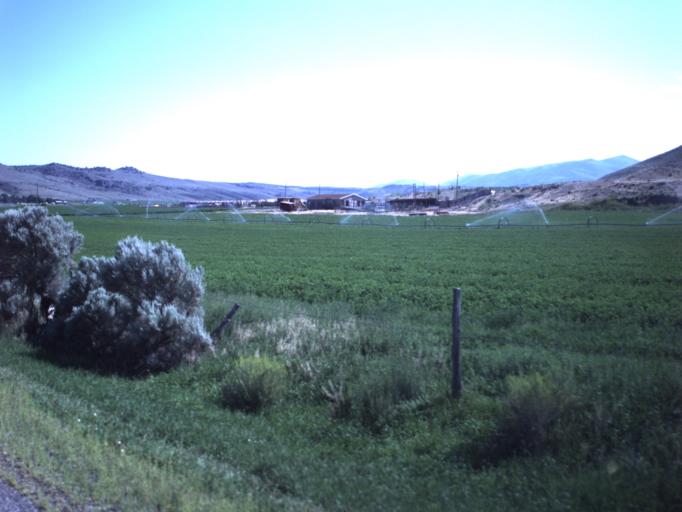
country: US
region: Utah
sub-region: Wayne County
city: Loa
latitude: 38.4452
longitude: -111.6158
